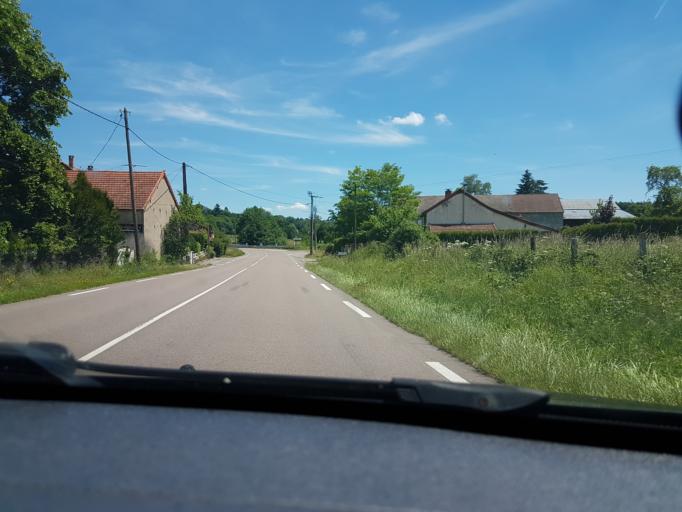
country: FR
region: Bourgogne
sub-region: Departement de Saone-et-Loire
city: Epinac
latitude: 46.9705
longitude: 4.5284
